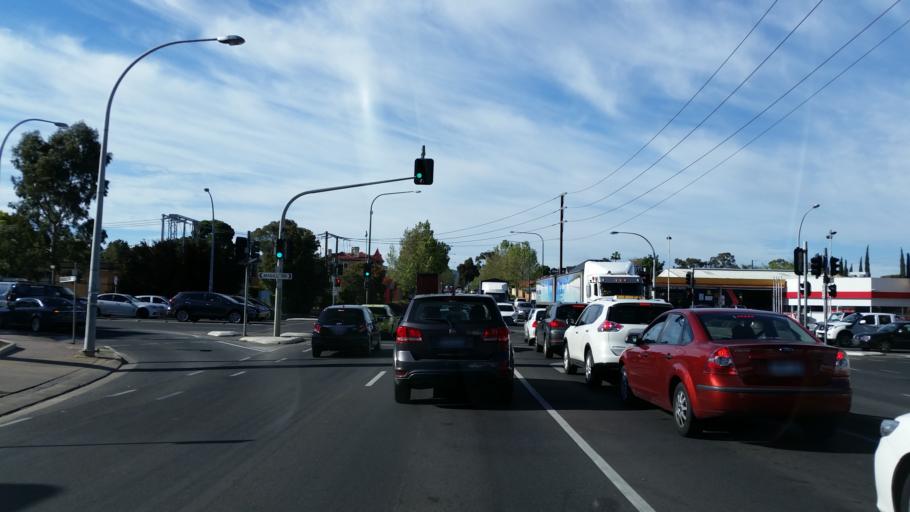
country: AU
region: South Australia
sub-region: Norwood Payneham St Peters
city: Trinity Gardens
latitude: -34.9144
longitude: 138.6405
